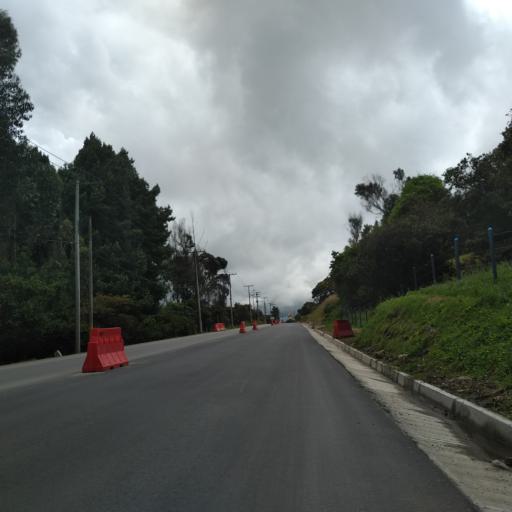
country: CO
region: Cundinamarca
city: La Calera
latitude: 4.6892
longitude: -73.9884
